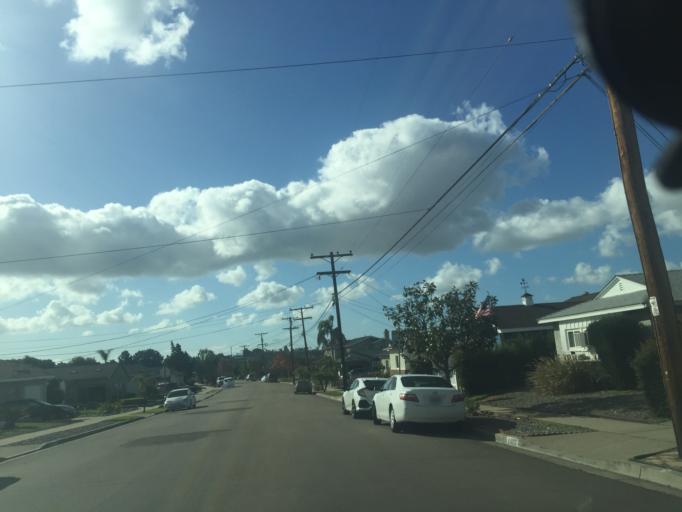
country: US
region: California
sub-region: San Diego County
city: La Mesa
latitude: 32.7911
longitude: -117.0881
